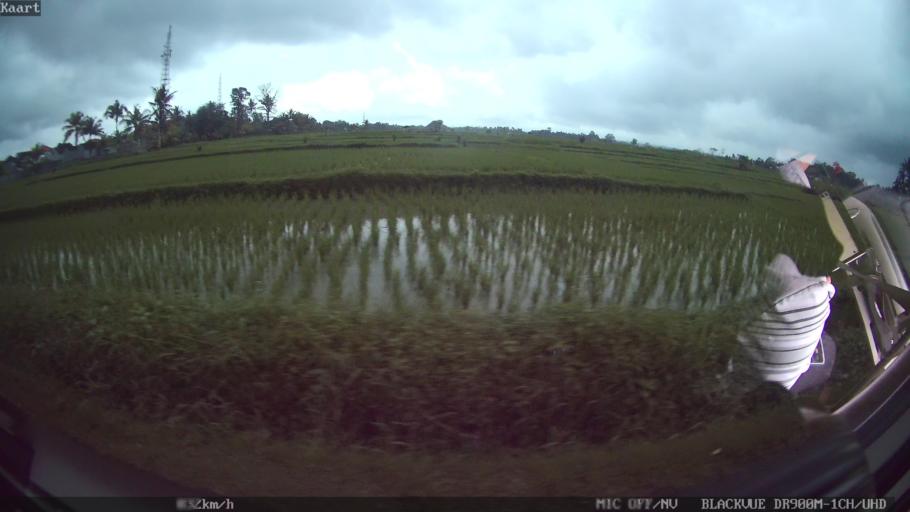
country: ID
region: Bali
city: Banjar Sempidi
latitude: -8.5211
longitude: 115.2107
